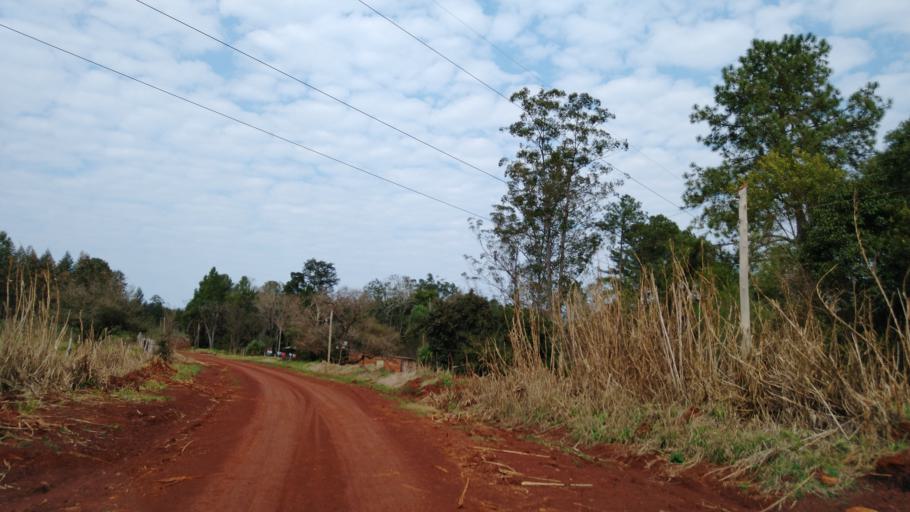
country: AR
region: Misiones
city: Capiovi
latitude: -26.9458
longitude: -55.0679
